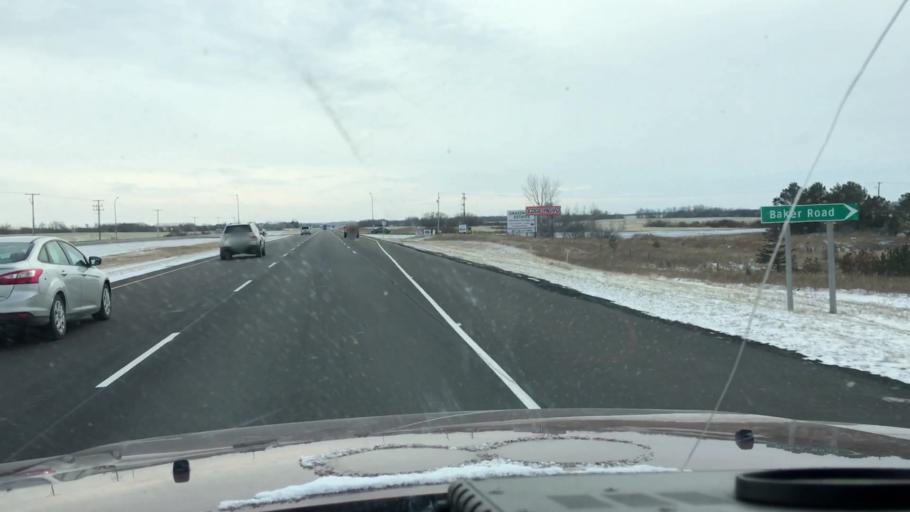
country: CA
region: Saskatchewan
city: Saskatoon
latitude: 52.0290
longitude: -106.5832
